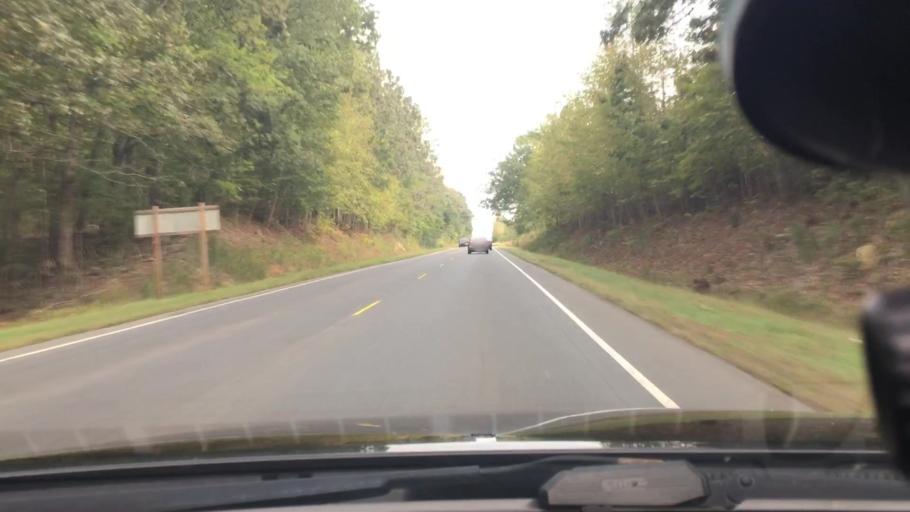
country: US
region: North Carolina
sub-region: Montgomery County
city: Mount Gilead
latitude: 35.3097
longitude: -80.0429
